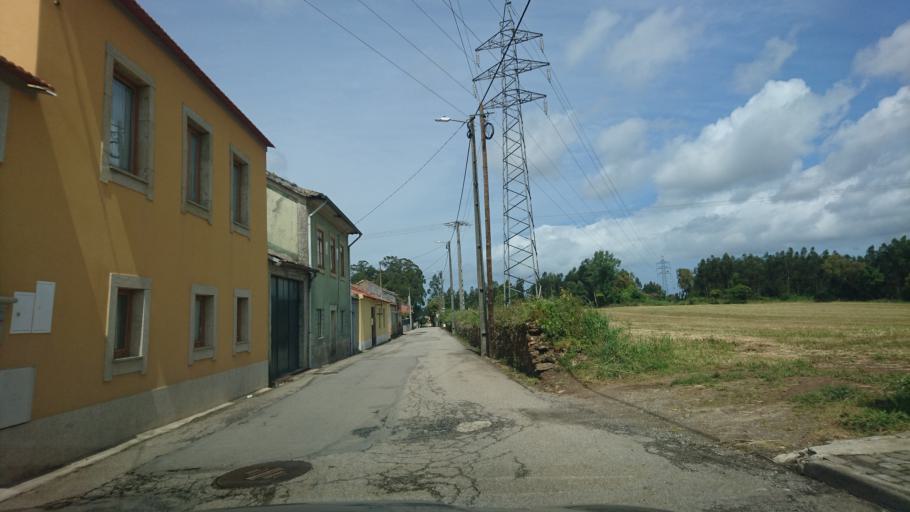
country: PT
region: Aveiro
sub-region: Santa Maria da Feira
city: Rio Meao
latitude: 40.9237
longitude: -8.5839
